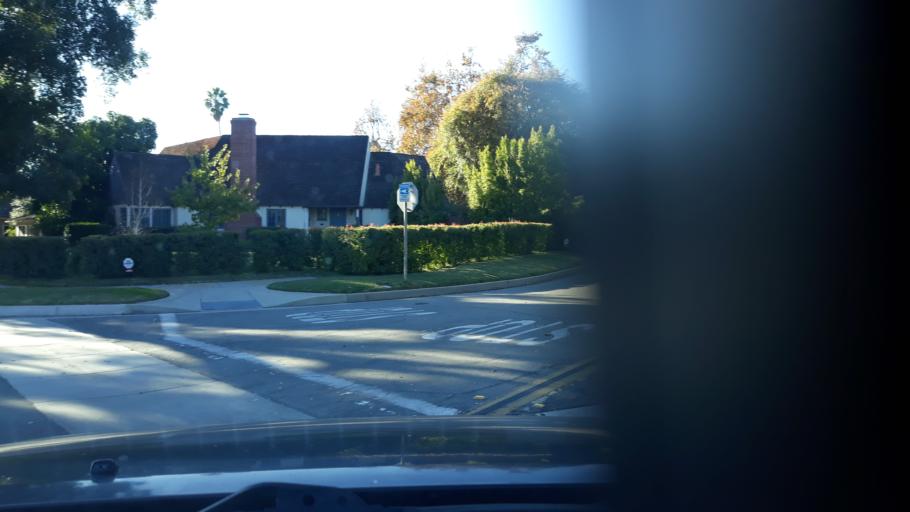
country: US
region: California
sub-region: Los Angeles County
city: San Marino
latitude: 34.1204
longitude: -118.0955
